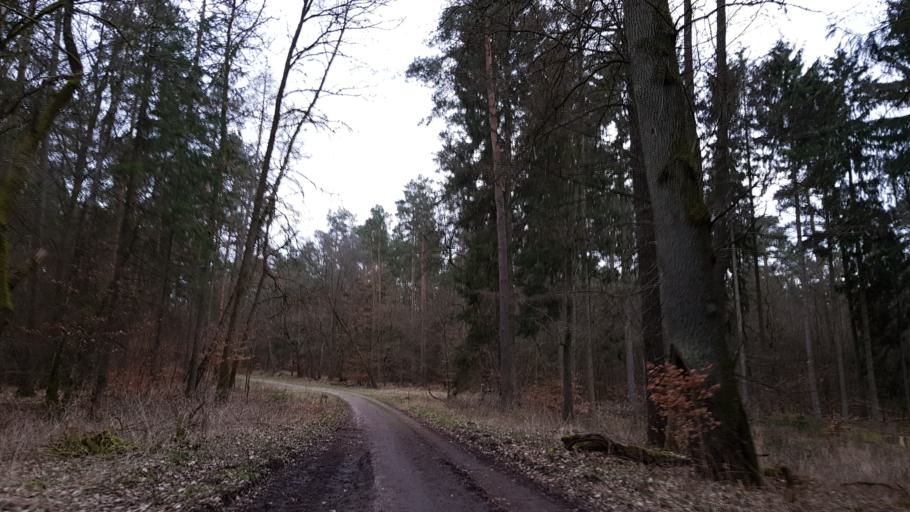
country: DE
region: Lower Saxony
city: Deutsch Evern
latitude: 53.2178
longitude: 10.4369
